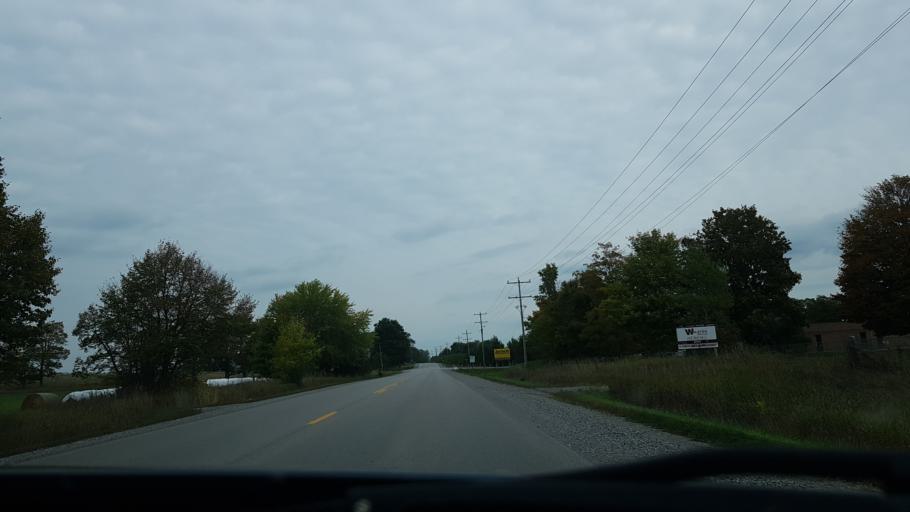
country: CA
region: Ontario
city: Omemee
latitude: 44.5190
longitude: -78.7974
